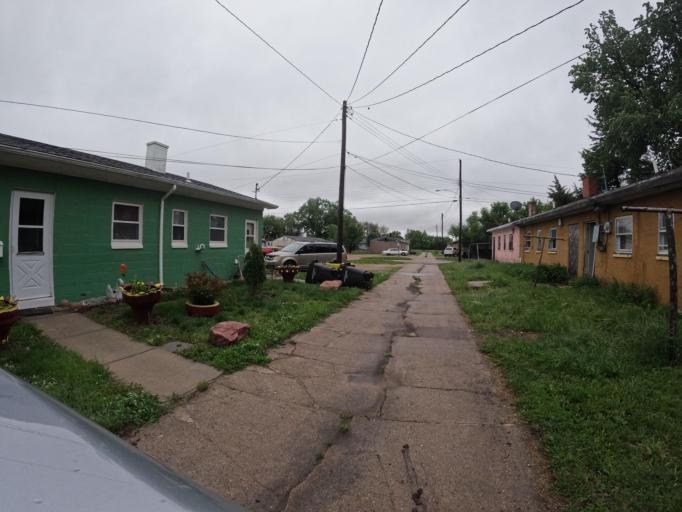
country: US
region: Nebraska
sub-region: Clay County
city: Harvard
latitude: 40.6268
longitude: -98.0930
